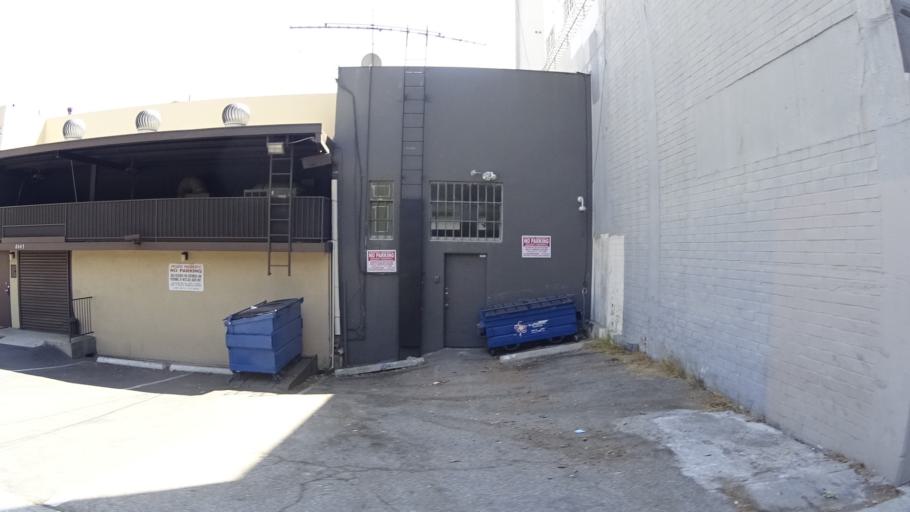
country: US
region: California
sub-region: Los Angeles County
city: West Hollywood
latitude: 34.0765
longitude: -118.3750
